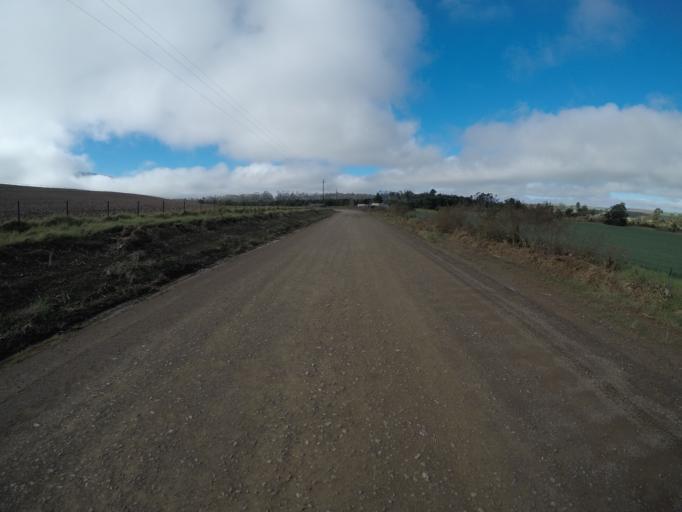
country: ZA
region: Western Cape
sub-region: Overberg District Municipality
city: Caledon
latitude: -34.1172
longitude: 19.7847
